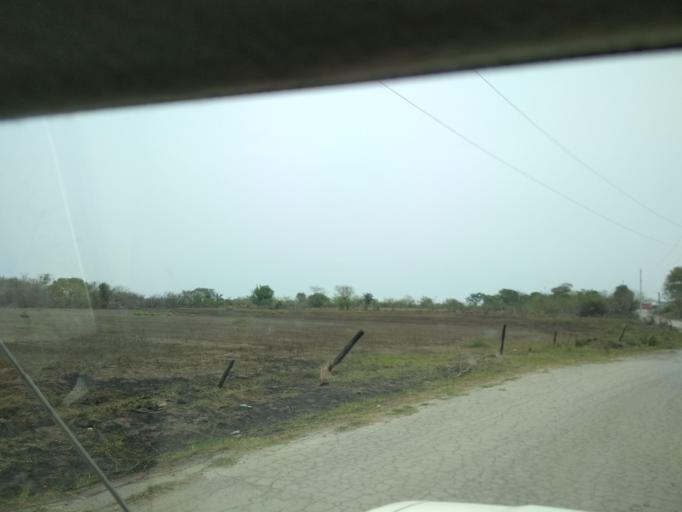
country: MX
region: Veracruz
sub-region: Veracruz
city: Delfino Victoria (Santa Fe)
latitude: 19.2012
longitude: -96.2583
